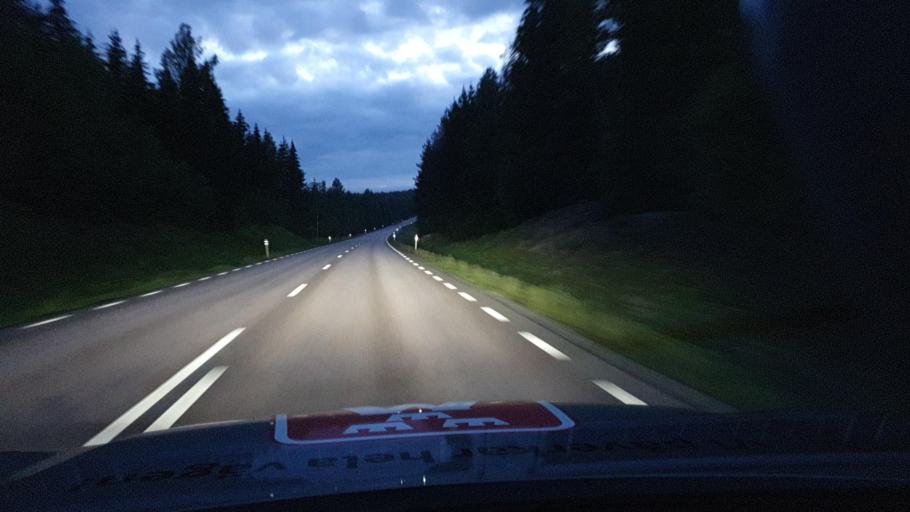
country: SE
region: Vaermland
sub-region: Storfors Kommun
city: Storfors
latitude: 59.4558
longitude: 14.3695
